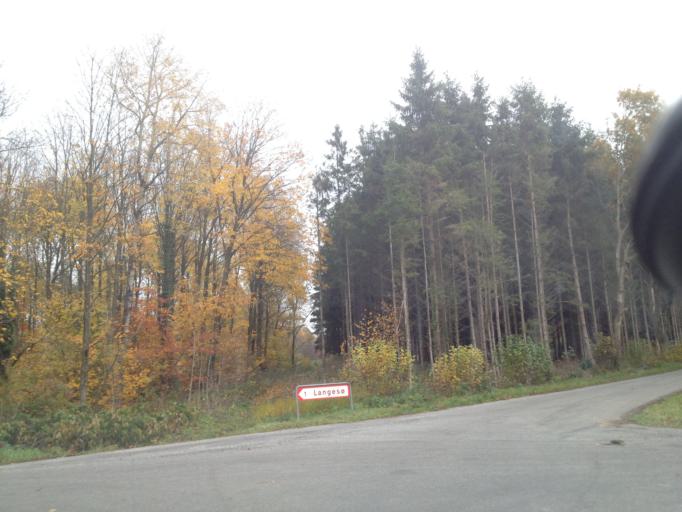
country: DK
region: South Denmark
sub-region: Assens Kommune
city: Vissenbjerg
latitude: 55.4260
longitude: 10.2024
